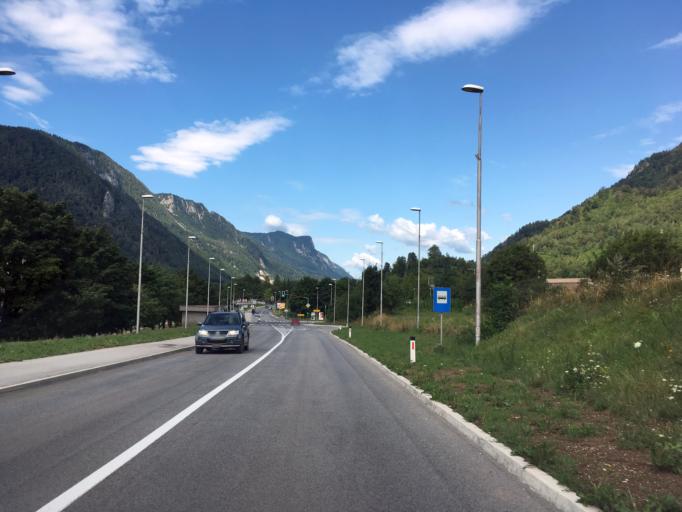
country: SI
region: Jesenice
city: Slovenski Javornik
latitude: 46.4259
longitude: 14.0946
